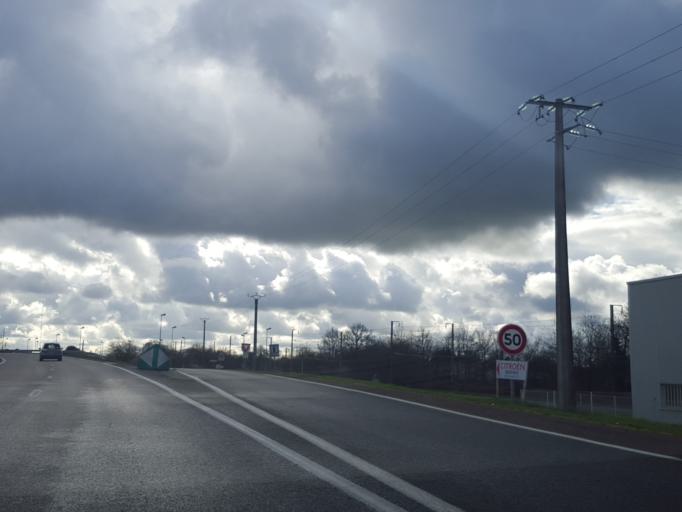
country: FR
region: Pays de la Loire
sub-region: Departement de la Vendee
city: Mouilleron-le-Captif
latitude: 46.7334
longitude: -1.4327
